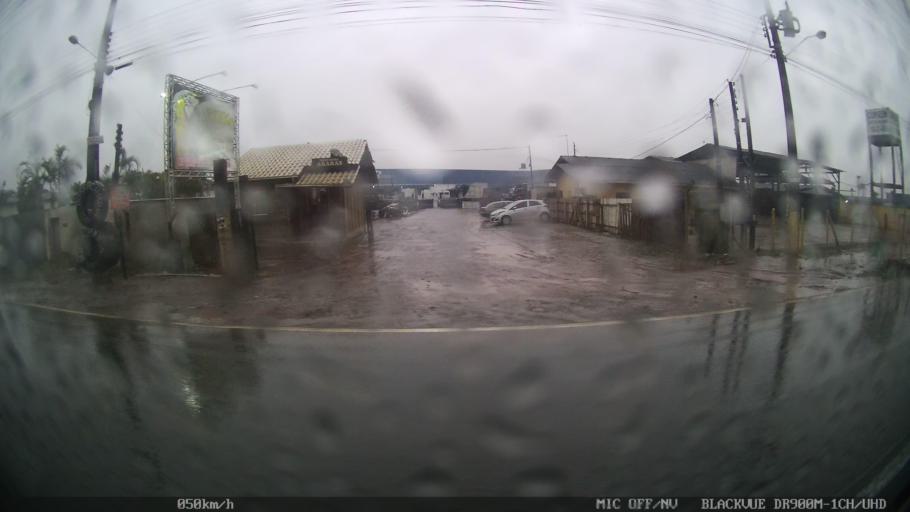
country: BR
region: Santa Catarina
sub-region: Navegantes
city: Navegantes
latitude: -26.8615
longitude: -48.6826
